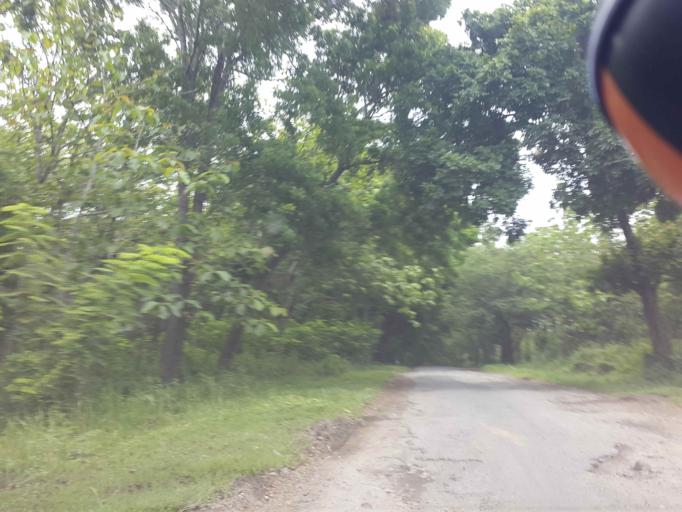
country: ID
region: East Java
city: Ponorogo
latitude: -7.7824
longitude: 111.3564
